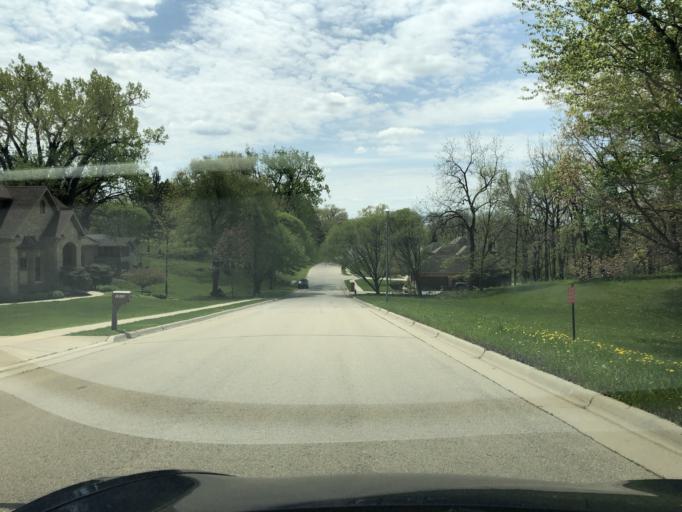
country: US
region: Iowa
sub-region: Dubuque County
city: Dubuque
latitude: 42.4783
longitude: -90.6629
